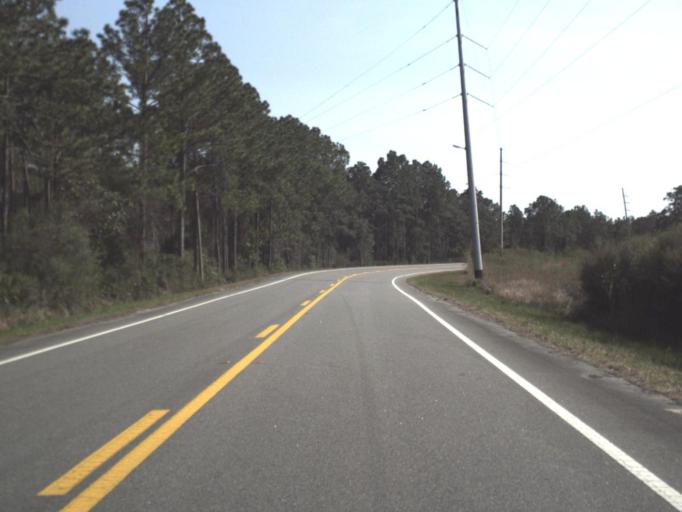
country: US
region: Florida
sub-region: Franklin County
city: Carrabelle
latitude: 29.9433
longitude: -84.5009
